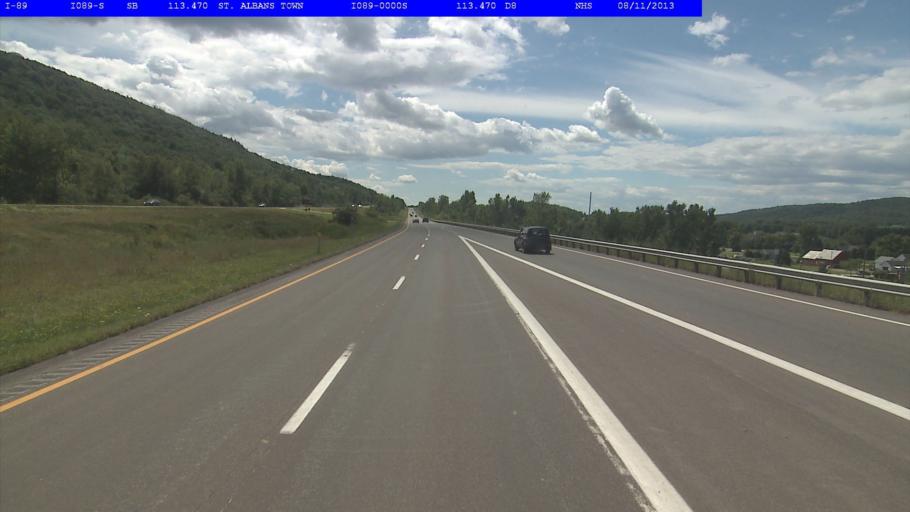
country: US
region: Vermont
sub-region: Franklin County
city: Saint Albans
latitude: 44.7911
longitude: -73.0717
